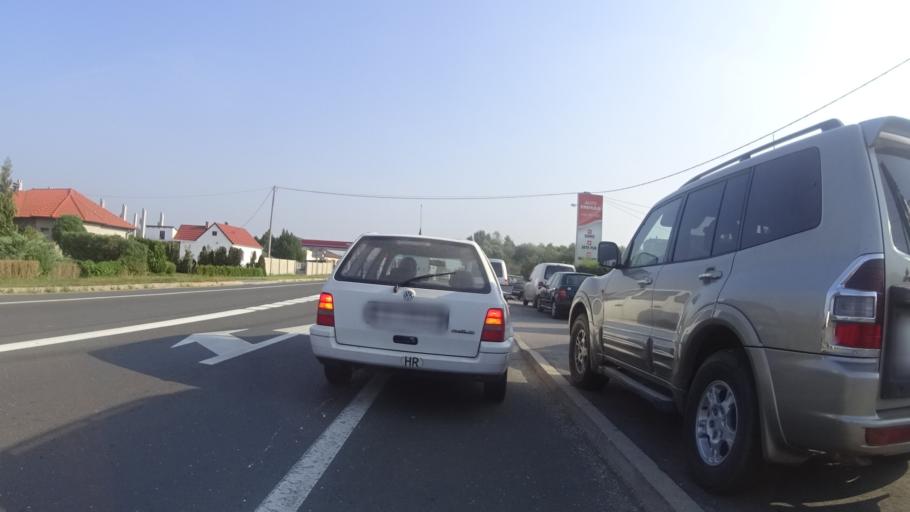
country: HR
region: Varazdinska
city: Varazdin
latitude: 46.3320
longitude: 16.3603
